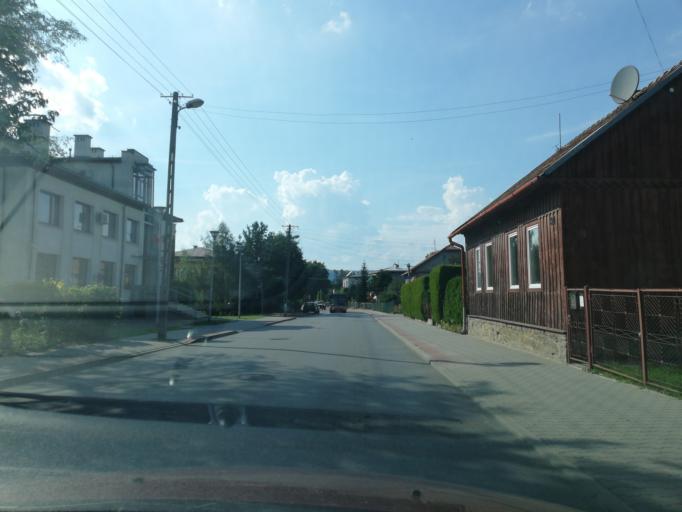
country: PL
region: Lesser Poland Voivodeship
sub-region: Powiat nowosadecki
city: Nowy Sacz
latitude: 49.6299
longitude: 20.6982
